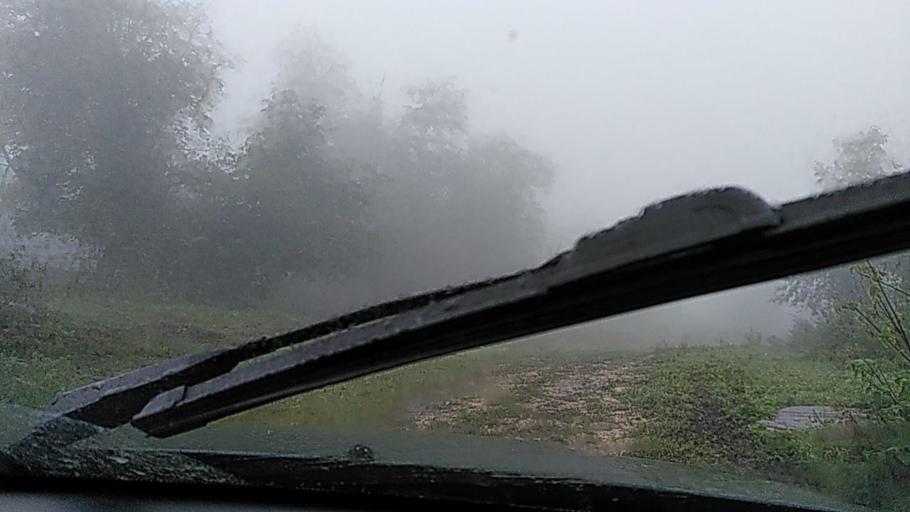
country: RU
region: Kabardino-Balkariya
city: Belaya Rechka
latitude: 43.3558
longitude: 43.4003
